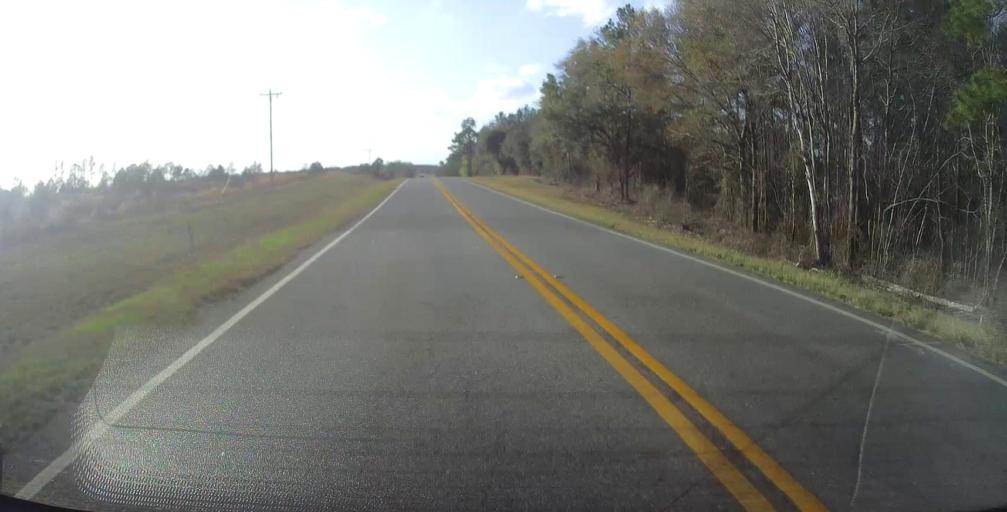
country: US
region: Georgia
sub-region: Tattnall County
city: Reidsville
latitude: 32.1290
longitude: -82.2142
